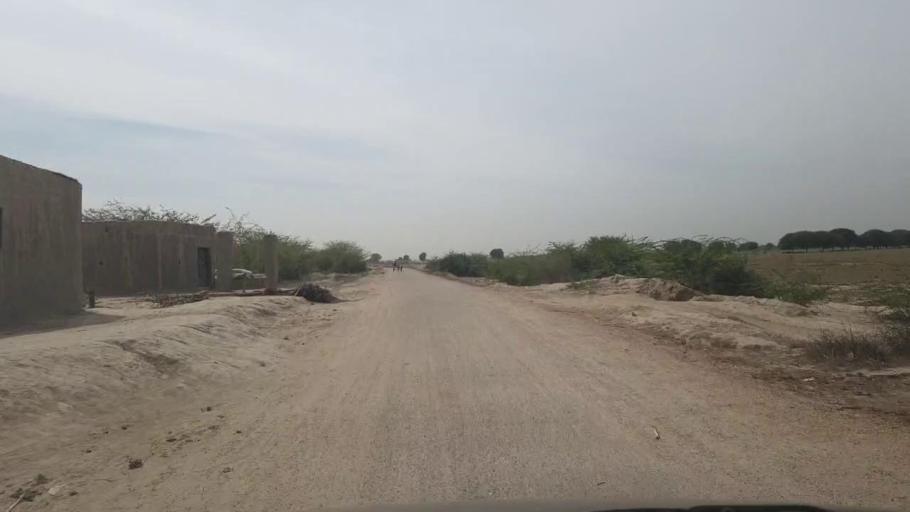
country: PK
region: Sindh
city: Umarkot
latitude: 25.2405
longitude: 69.7142
